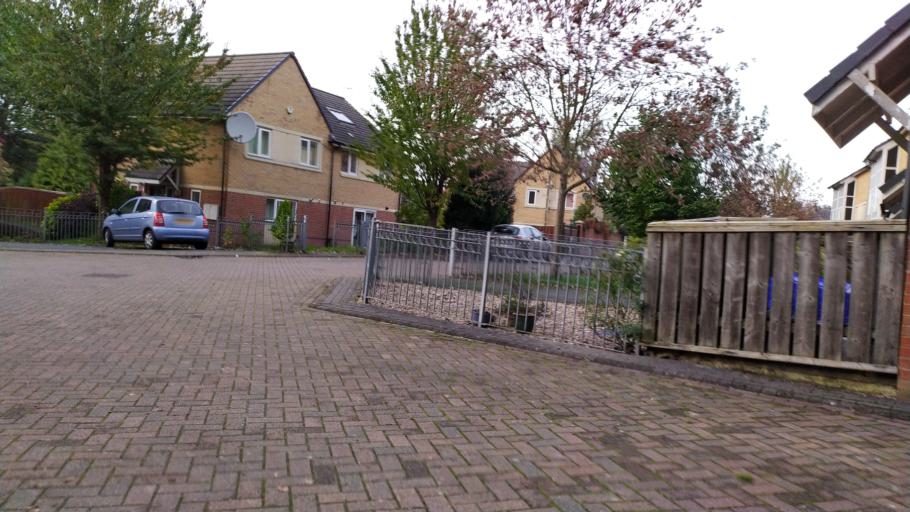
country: GB
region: England
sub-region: City and Borough of Leeds
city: Leeds
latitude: 53.8206
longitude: -1.5913
